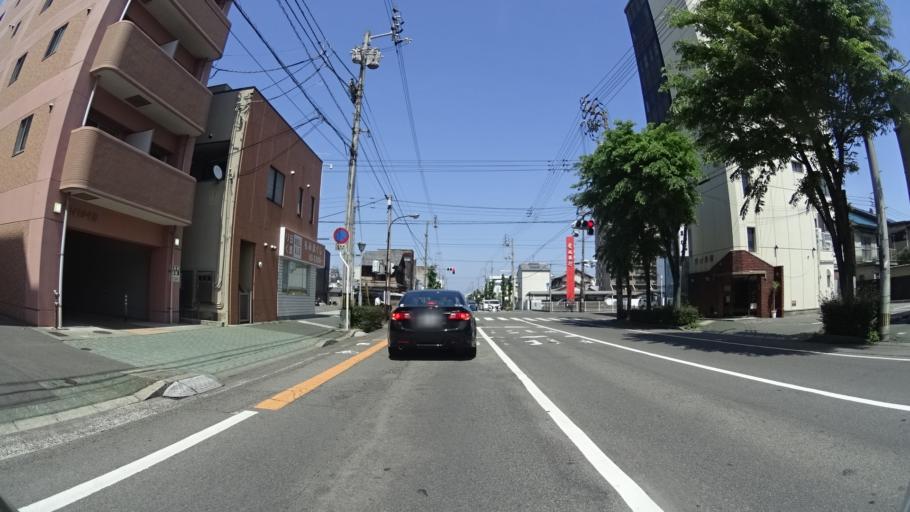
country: JP
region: Ehime
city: Saijo
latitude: 34.0599
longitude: 133.0031
